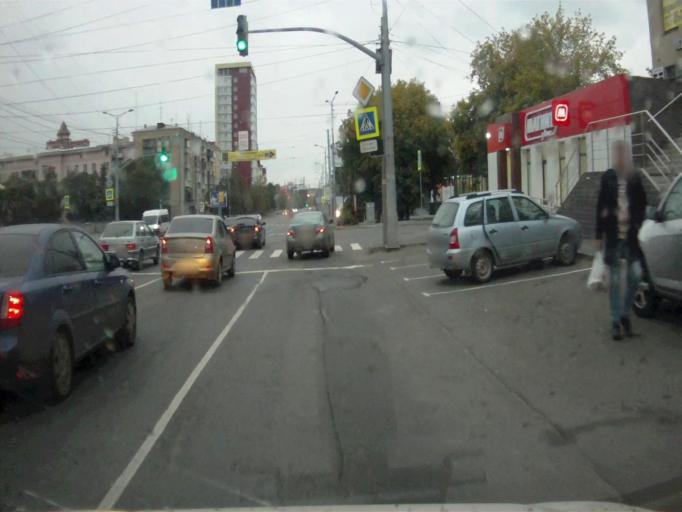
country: RU
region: Chelyabinsk
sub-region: Gorod Chelyabinsk
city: Chelyabinsk
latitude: 55.1625
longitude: 61.4116
